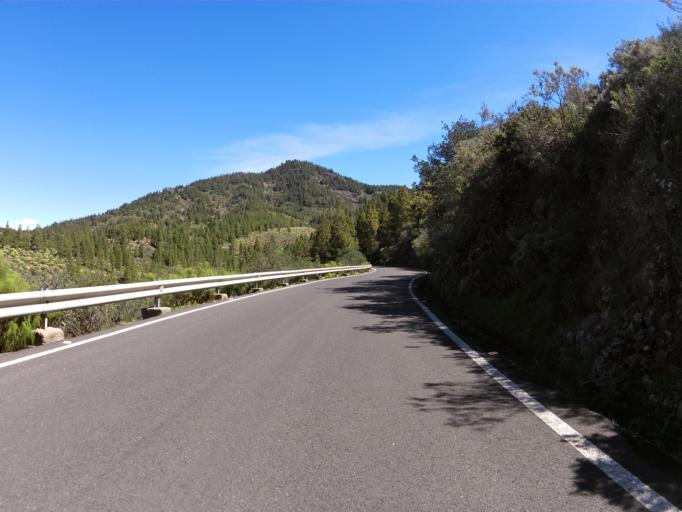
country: ES
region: Canary Islands
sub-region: Provincia de Las Palmas
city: Artenara
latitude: 28.0169
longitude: -15.6733
